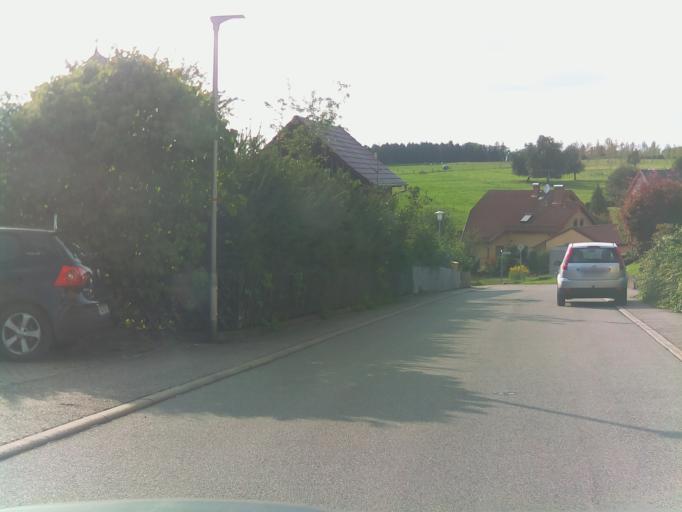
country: DE
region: Hesse
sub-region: Regierungsbezirk Darmstadt
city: Hesseneck
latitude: 49.5747
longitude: 9.0889
